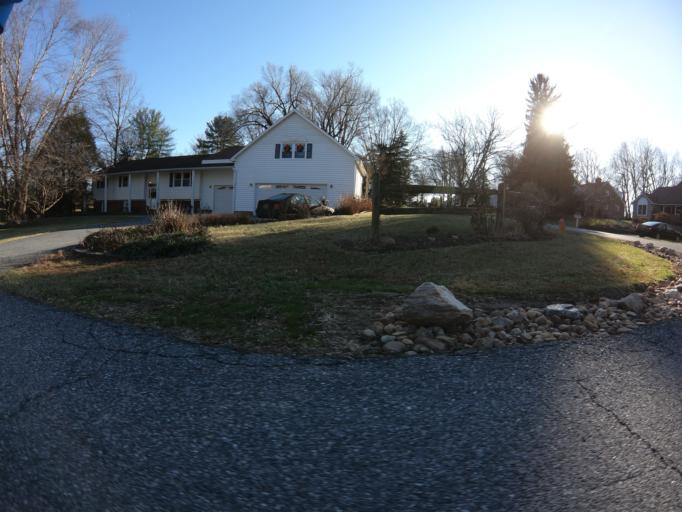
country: US
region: Maryland
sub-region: Howard County
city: Columbia
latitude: 39.2495
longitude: -76.8643
